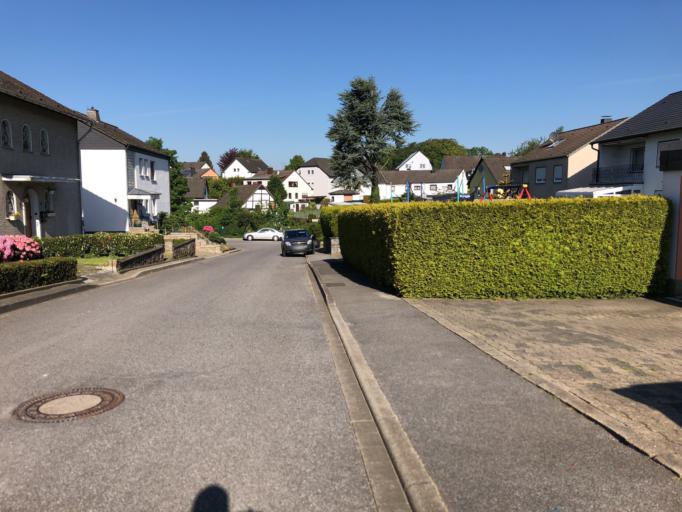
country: DE
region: North Rhine-Westphalia
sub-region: Regierungsbezirk Arnsberg
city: Frondenberg
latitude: 51.4777
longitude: 7.7283
